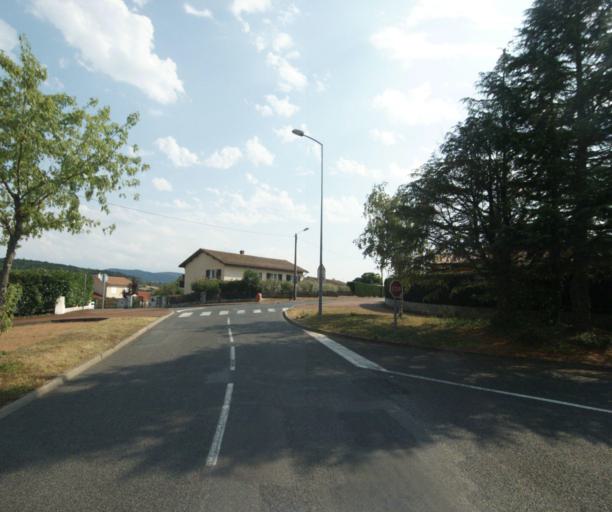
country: FR
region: Rhone-Alpes
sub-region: Departement du Rhone
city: Saint-Germain-Nuelles
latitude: 45.8324
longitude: 4.6087
